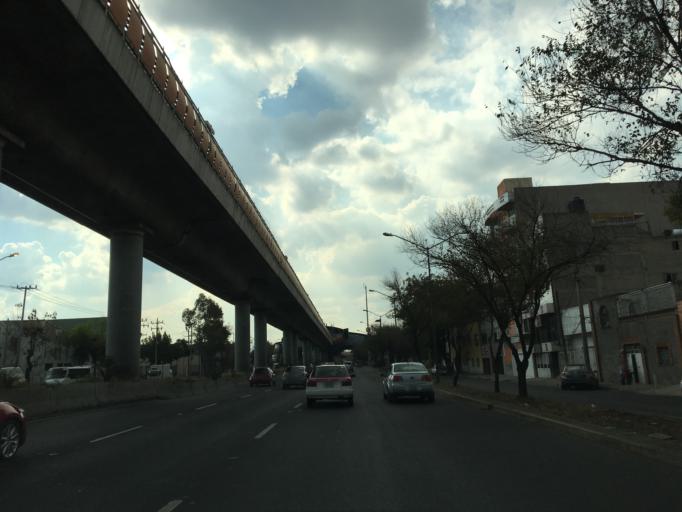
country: MX
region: Mexico City
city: Venustiano Carranza
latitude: 19.4378
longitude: -99.1012
